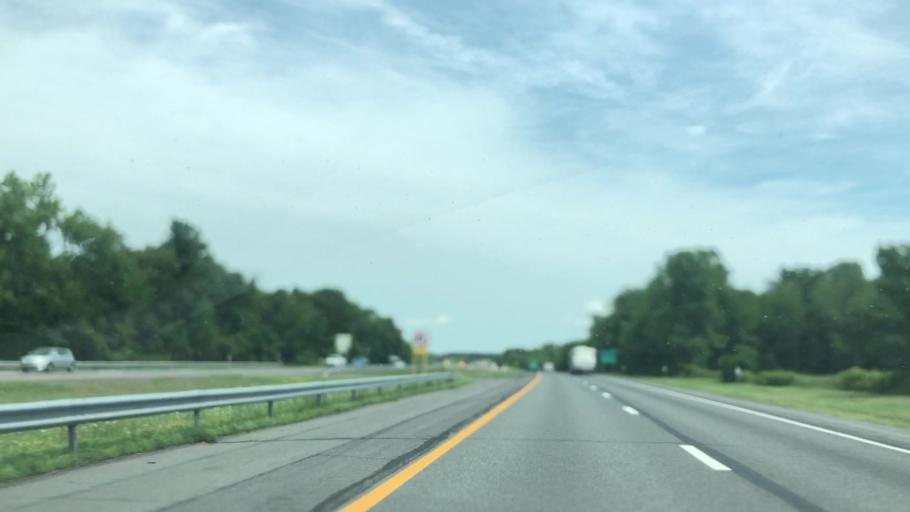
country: US
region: New York
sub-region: Albany County
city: Ravena
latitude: 42.5035
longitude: -73.7935
